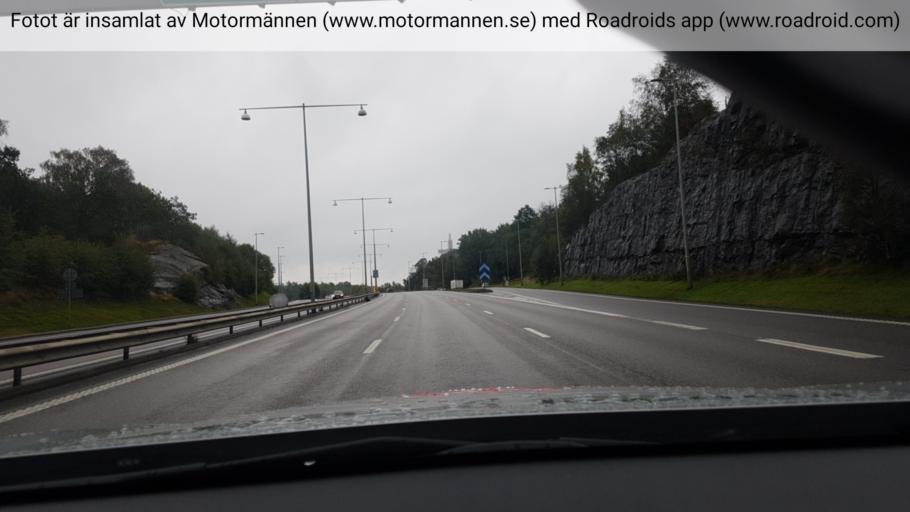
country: SE
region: Vaestra Goetaland
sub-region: Molndal
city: Moelndal
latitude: 57.6801
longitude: 12.0199
